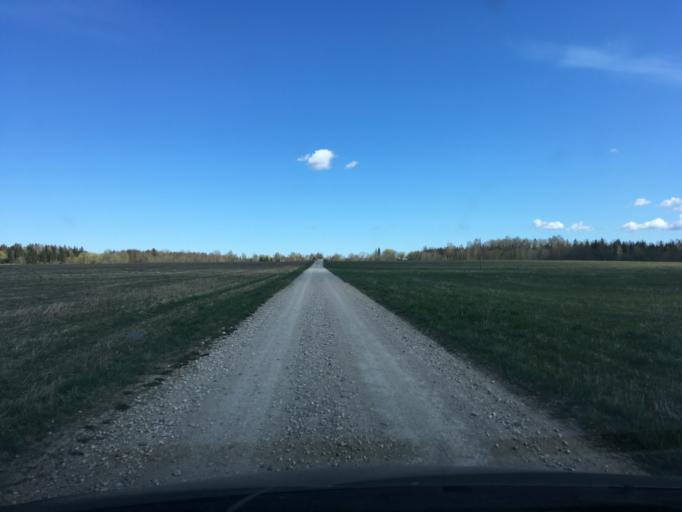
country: EE
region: Harju
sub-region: Raasiku vald
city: Raasiku
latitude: 59.2193
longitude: 25.2104
